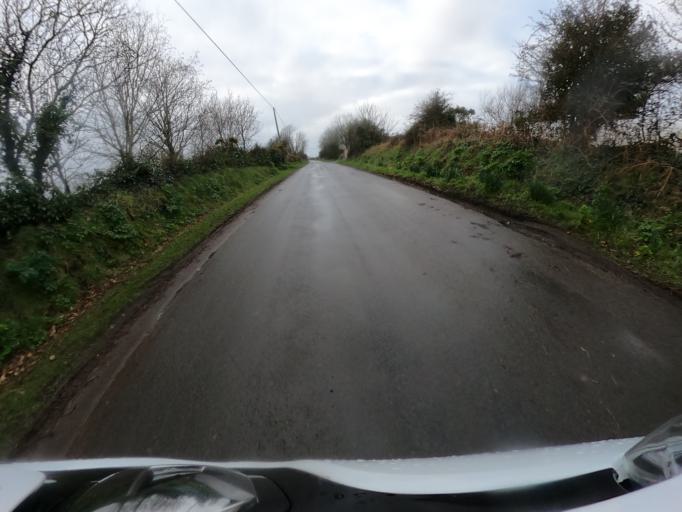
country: IM
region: Ramsey
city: Ramsey
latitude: 54.3635
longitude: -4.5047
